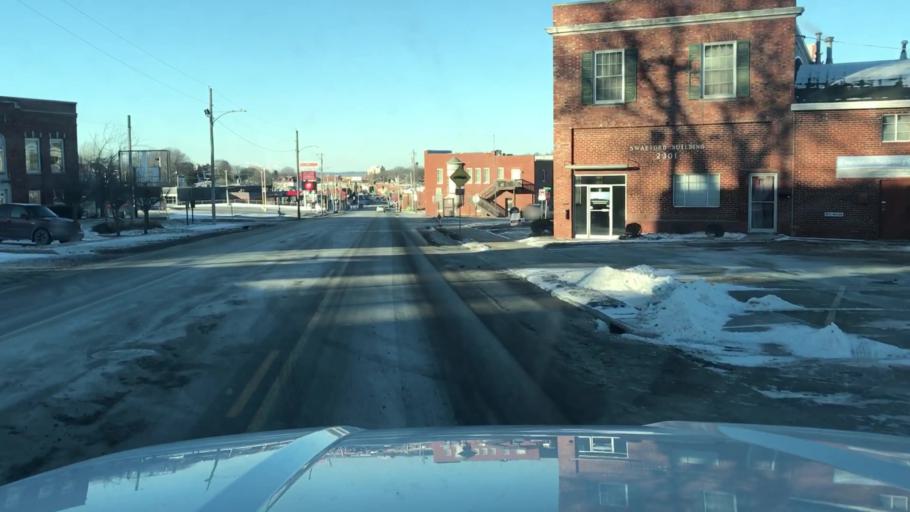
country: US
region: Missouri
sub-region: Buchanan County
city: Saint Joseph
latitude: 39.7761
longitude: -94.8323
